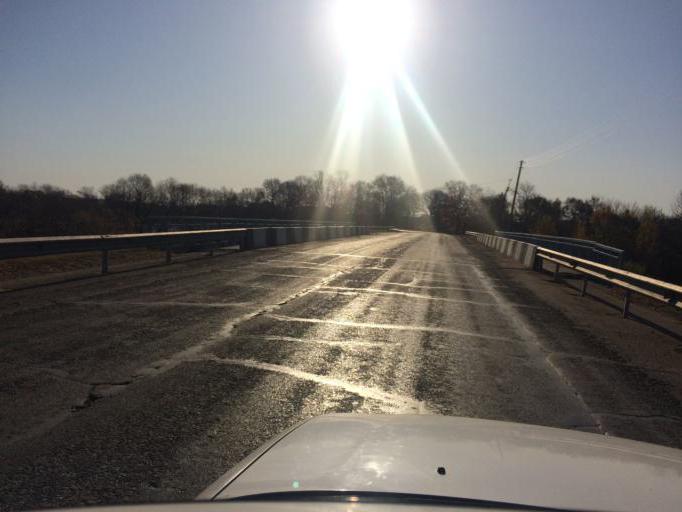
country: RU
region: Primorskiy
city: Dal'nerechensk
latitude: 45.9144
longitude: 133.7890
